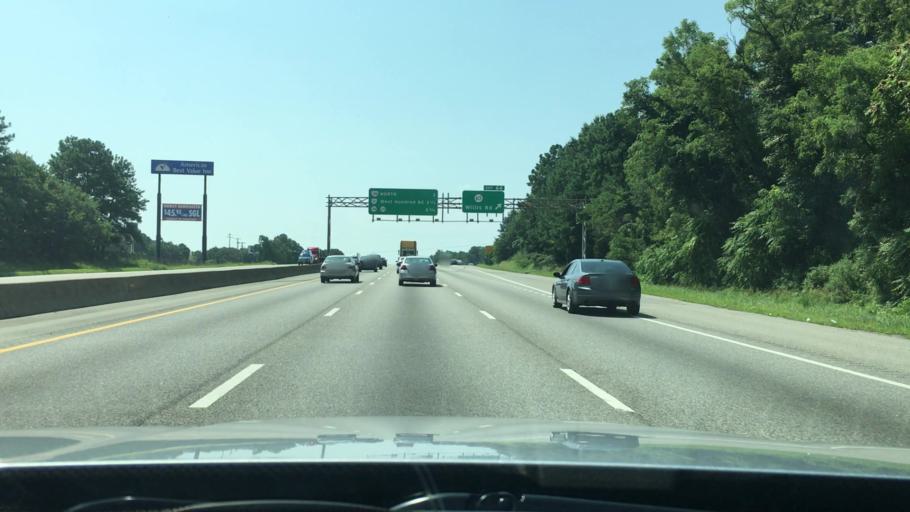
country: US
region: Virginia
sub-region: Chesterfield County
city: Bellwood
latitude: 37.4048
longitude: -77.4254
